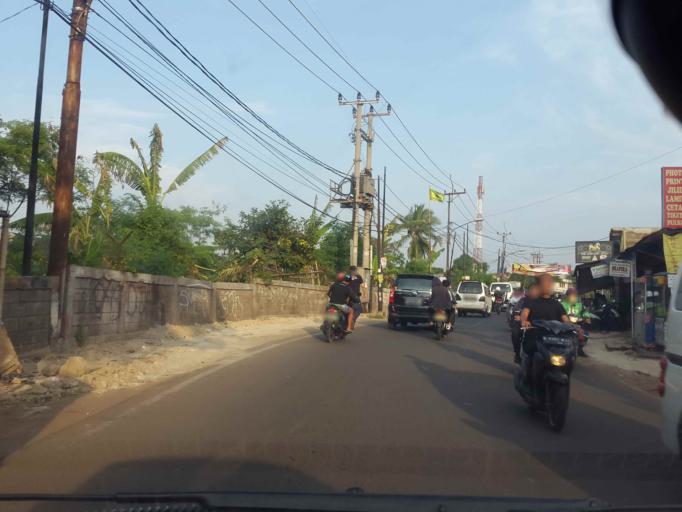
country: ID
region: Banten
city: South Tangerang
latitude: -6.2593
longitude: 106.7425
